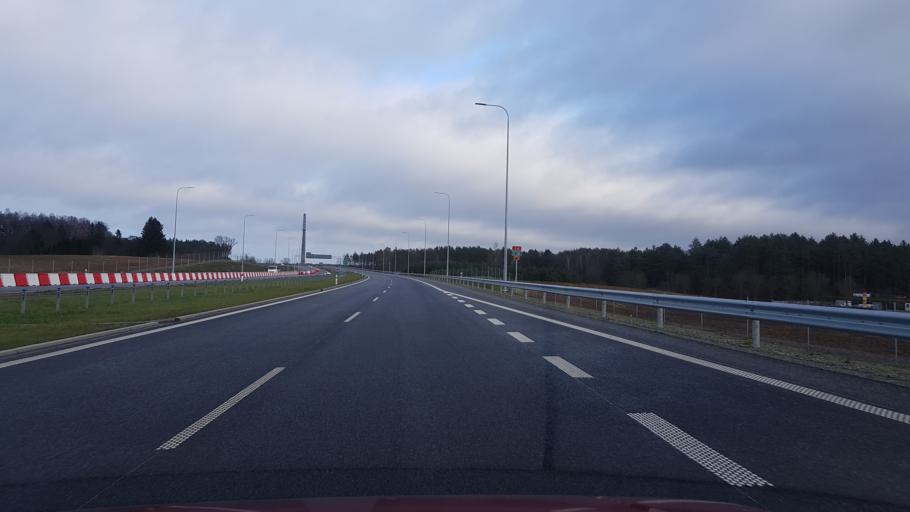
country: PL
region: West Pomeranian Voivodeship
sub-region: Powiat koszalinski
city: Sianow
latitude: 54.2405
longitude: 16.3249
